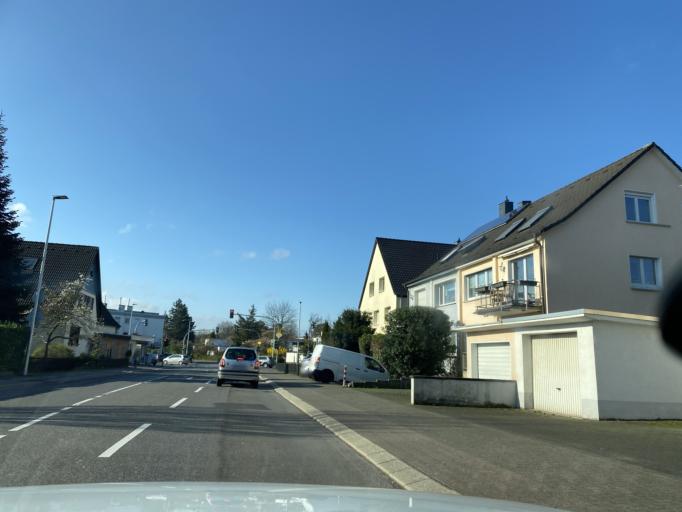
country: DE
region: North Rhine-Westphalia
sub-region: Regierungsbezirk Koln
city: Bergisch Gladbach
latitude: 51.0021
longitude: 7.1196
